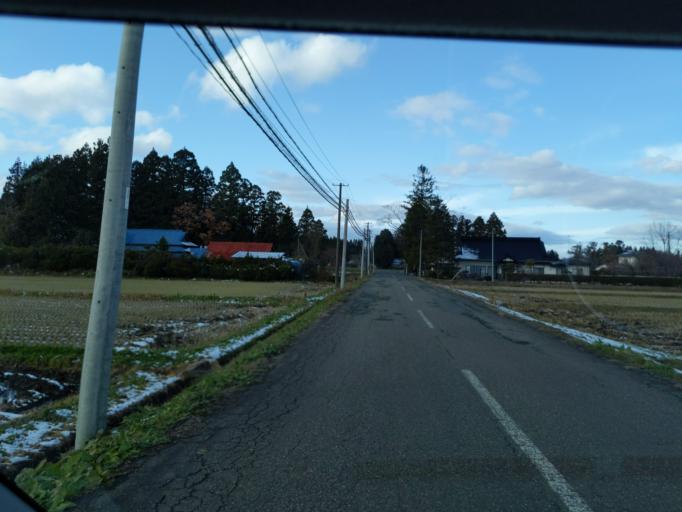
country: JP
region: Iwate
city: Kitakami
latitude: 39.2171
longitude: 141.0473
